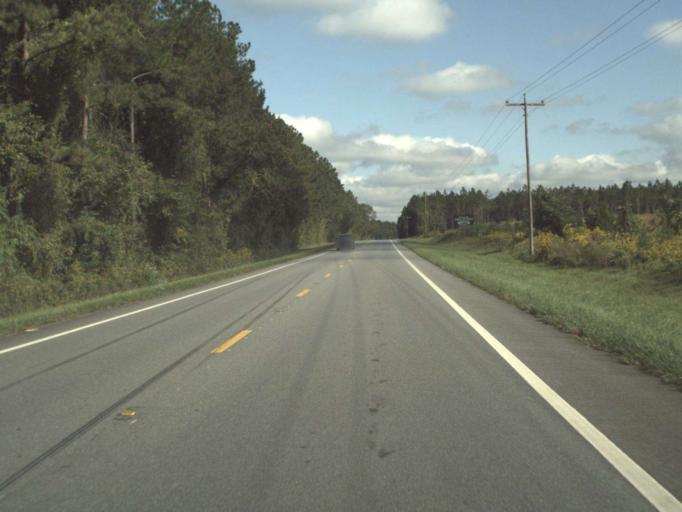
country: US
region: Florida
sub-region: Calhoun County
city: Blountstown
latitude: 30.3203
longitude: -85.1275
